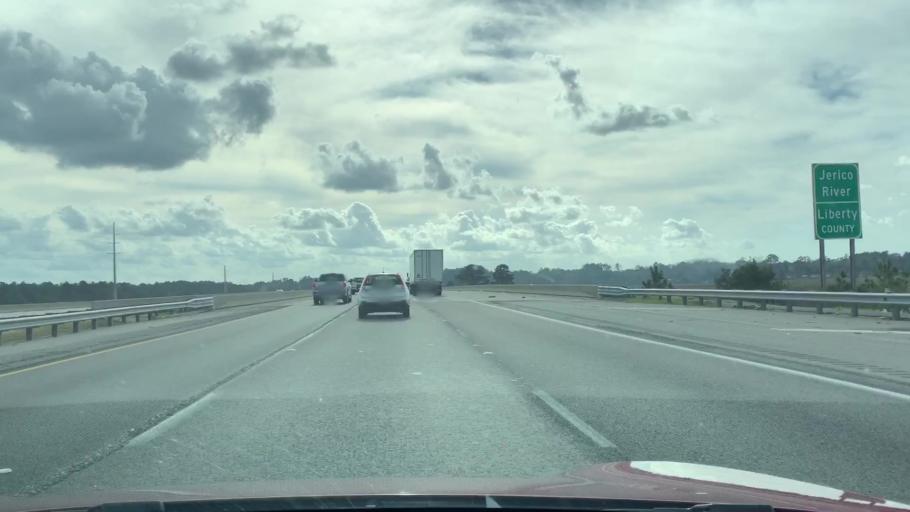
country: US
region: Georgia
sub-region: Liberty County
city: Midway
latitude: 31.8310
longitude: -81.3547
